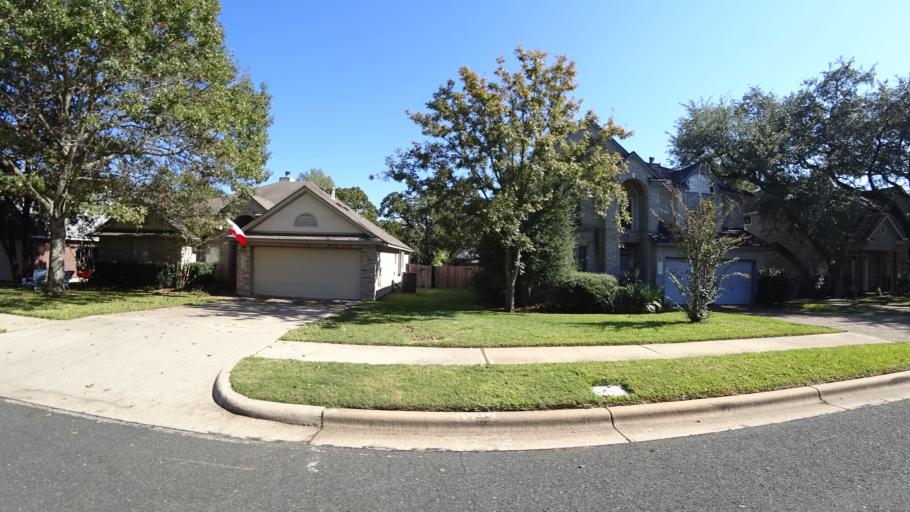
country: US
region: Texas
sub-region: Travis County
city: Shady Hollow
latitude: 30.2196
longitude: -97.8716
